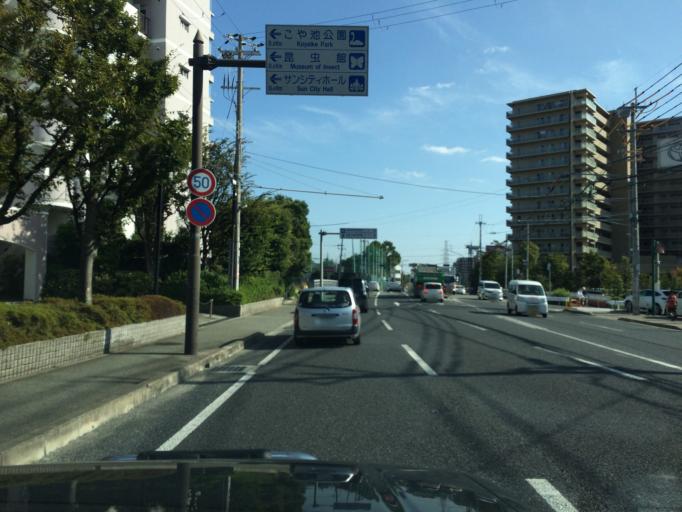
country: JP
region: Hyogo
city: Itami
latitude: 34.7875
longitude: 135.3827
